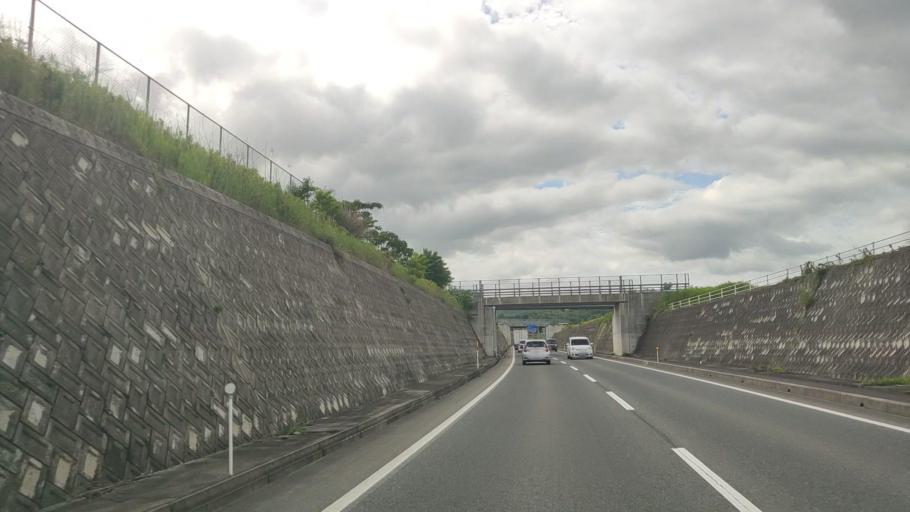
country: JP
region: Tottori
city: Yonago
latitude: 35.3862
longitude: 133.3848
